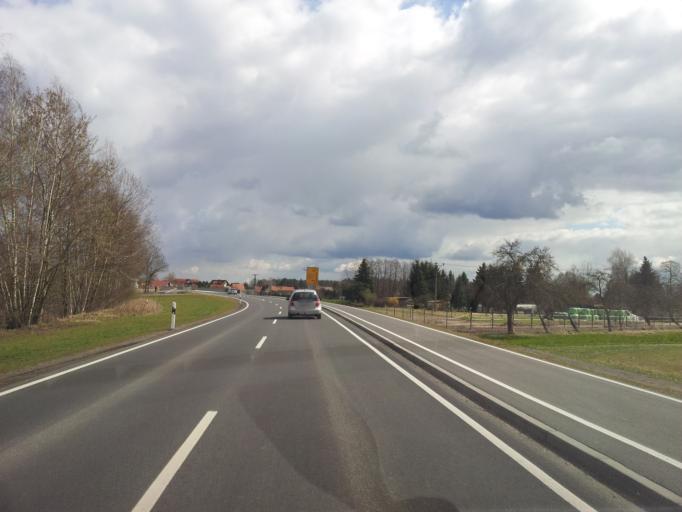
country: DE
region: Saxony
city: Wittichenau
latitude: 51.3850
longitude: 14.2554
